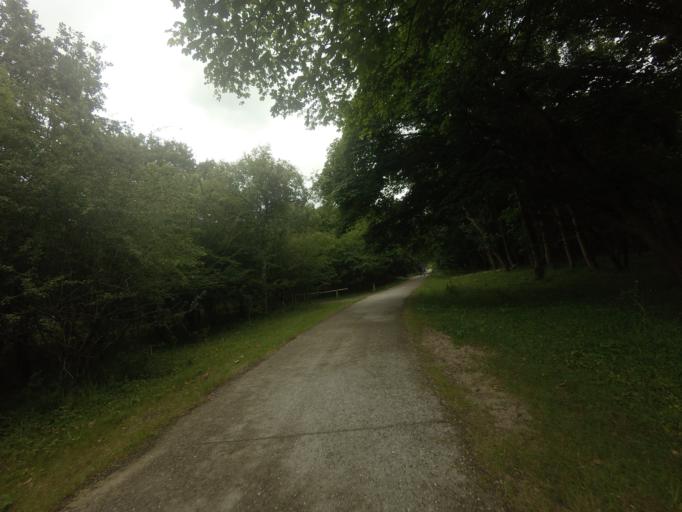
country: NL
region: North Holland
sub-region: Gemeente Bloemendaal
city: Bloemendaal
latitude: 52.4340
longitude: 4.5839
